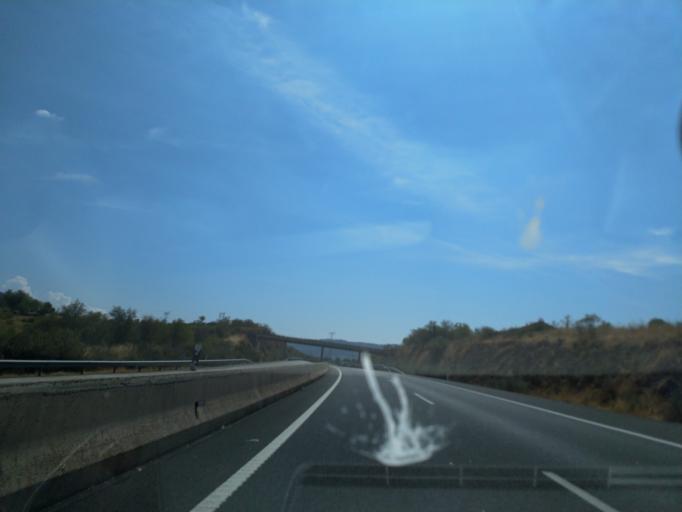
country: ES
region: Extremadura
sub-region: Provincia de Caceres
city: Casas de Miravete
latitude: 39.7457
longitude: -5.7264
